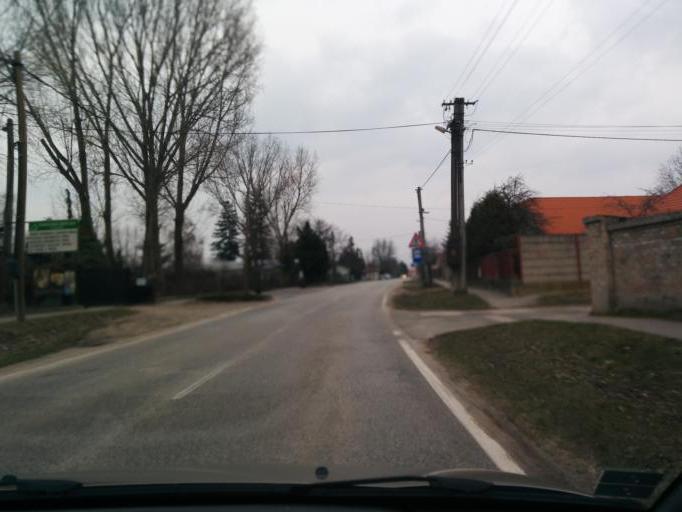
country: SK
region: Trnavsky
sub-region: Okres Galanta
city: Galanta
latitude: 48.2587
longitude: 17.8078
